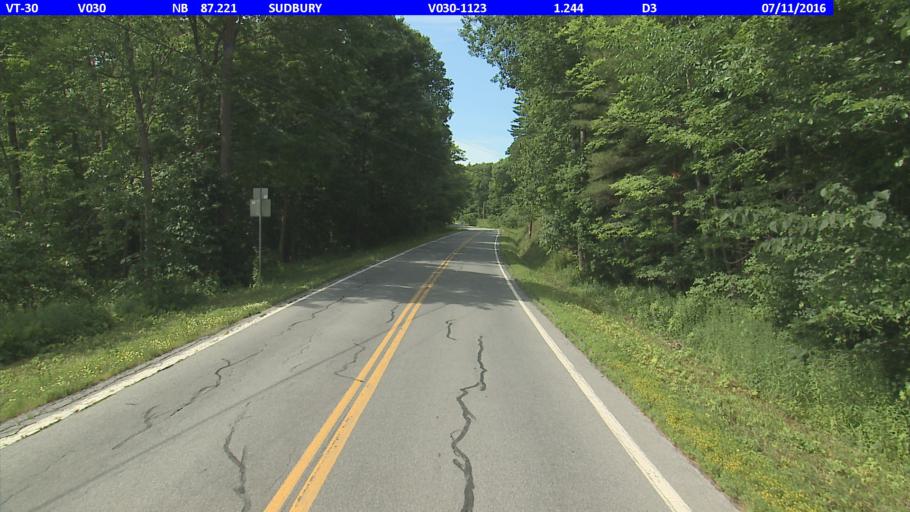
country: US
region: Vermont
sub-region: Rutland County
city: Brandon
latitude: 43.7670
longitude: -73.1974
